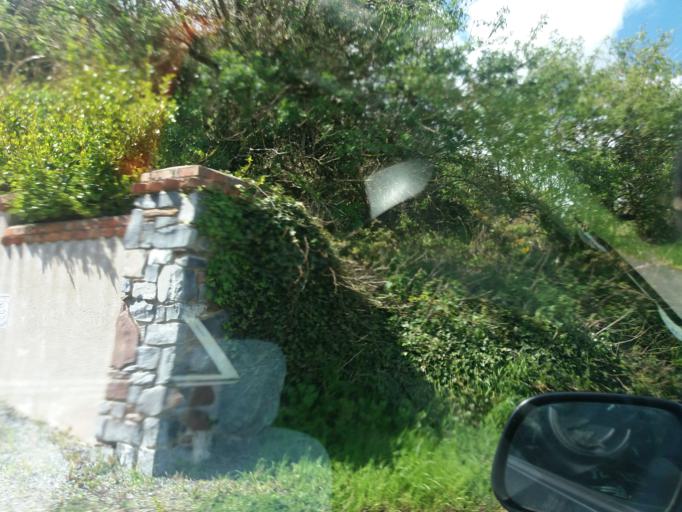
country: IE
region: Munster
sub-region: Waterford
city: Dunmore East
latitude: 52.2442
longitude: -6.9564
